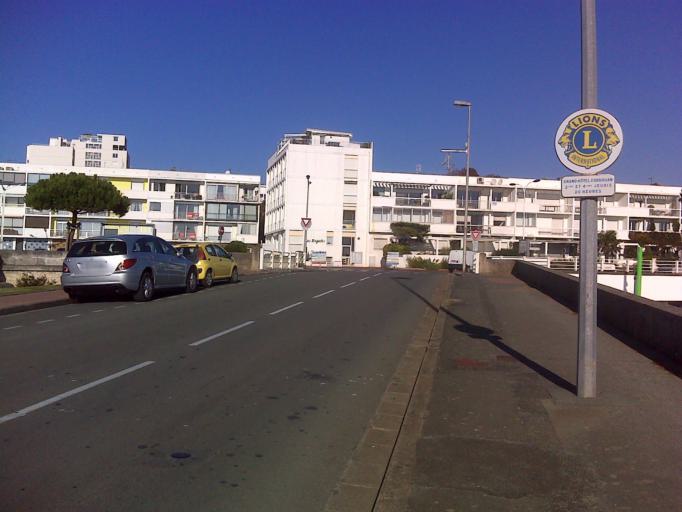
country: FR
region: Poitou-Charentes
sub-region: Departement de la Charente-Maritime
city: Royan
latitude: 45.6193
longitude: -1.0309
